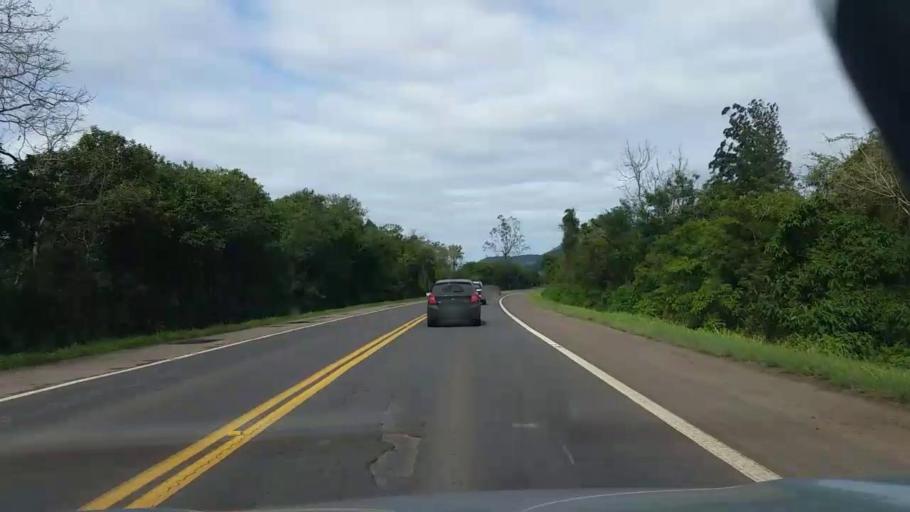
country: BR
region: Rio Grande do Sul
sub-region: Arroio Do Meio
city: Arroio do Meio
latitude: -29.3457
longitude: -52.0724
